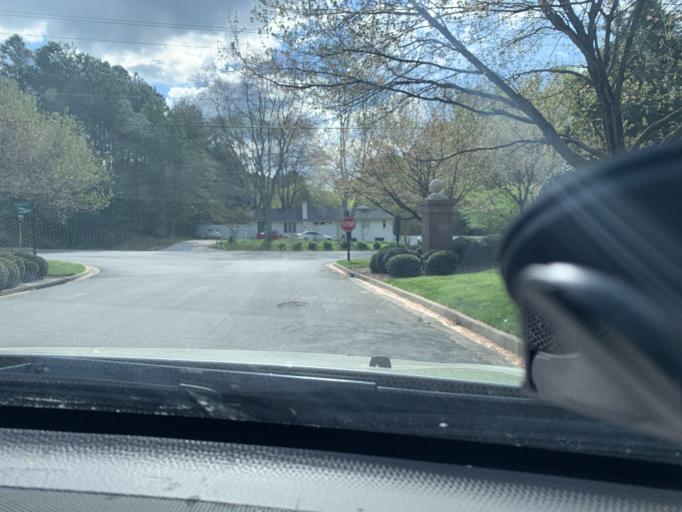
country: US
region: Virginia
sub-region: Henrico County
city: Tuckahoe
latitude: 37.5901
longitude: -77.6002
